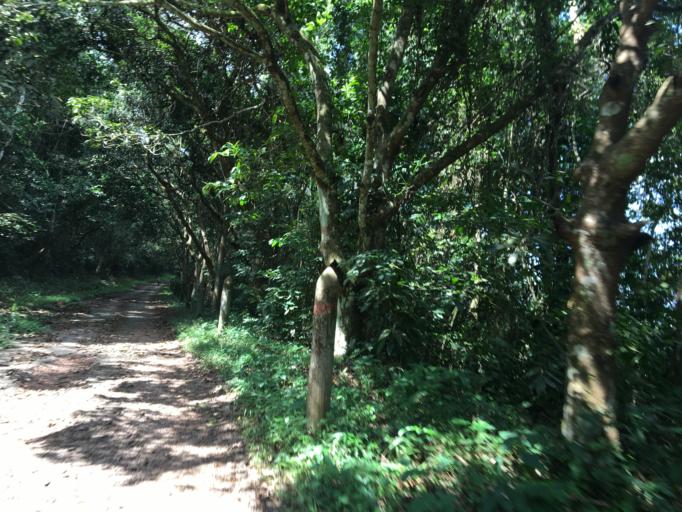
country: TG
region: Plateaux
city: Kpalime
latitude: 6.9537
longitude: 0.5841
